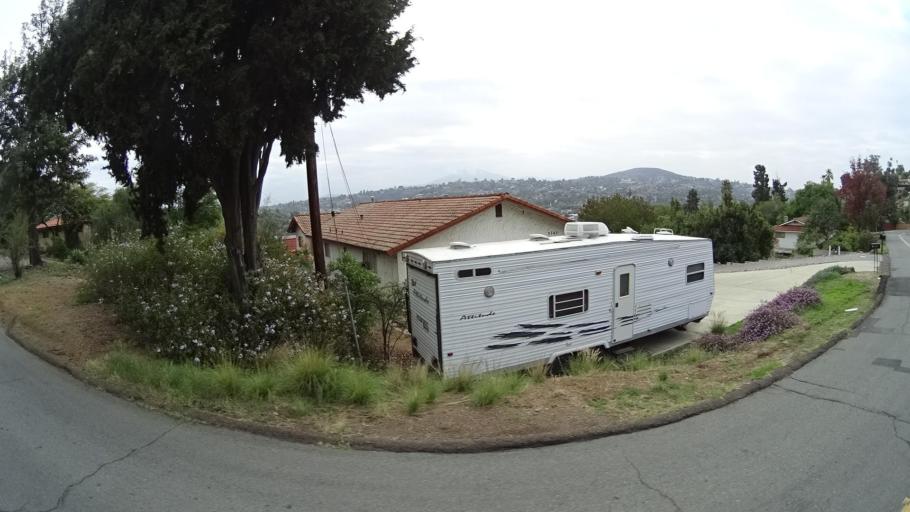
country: US
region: California
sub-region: San Diego County
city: Spring Valley
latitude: 32.7485
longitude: -117.0072
